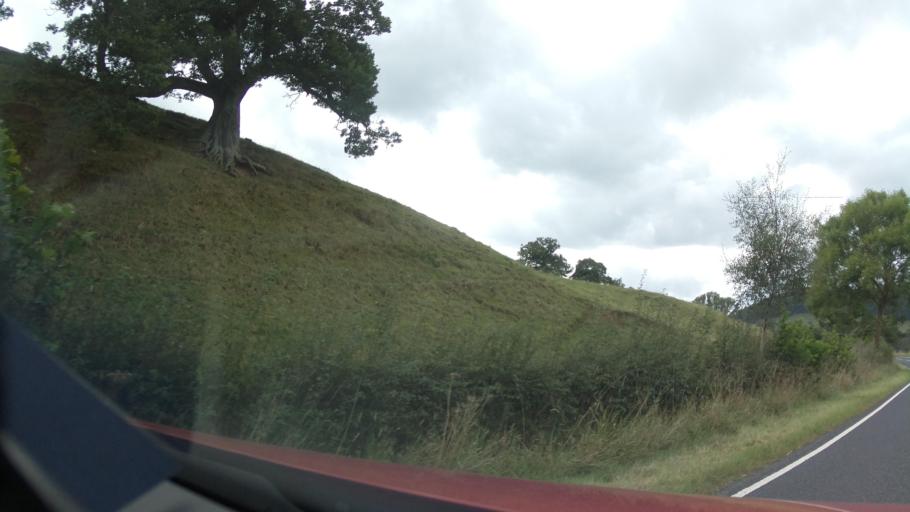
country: GB
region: England
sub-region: North Yorkshire
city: Leyburn
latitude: 54.4047
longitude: -1.8169
